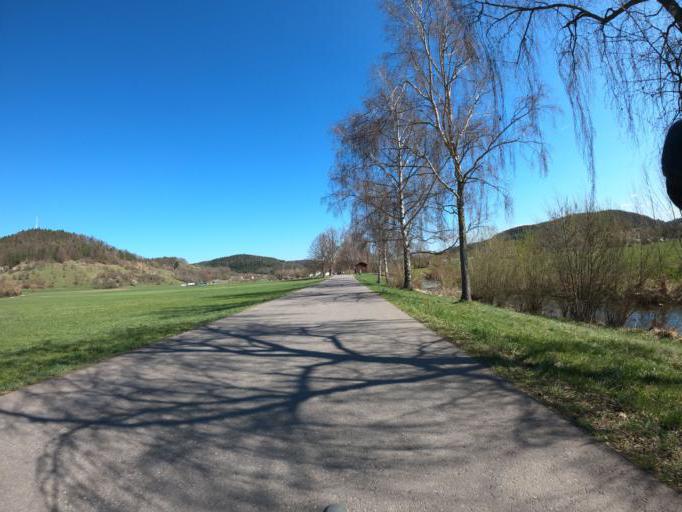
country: DE
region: Baden-Wuerttemberg
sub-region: Tuebingen Region
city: Rangendingen
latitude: 48.3850
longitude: 8.8881
